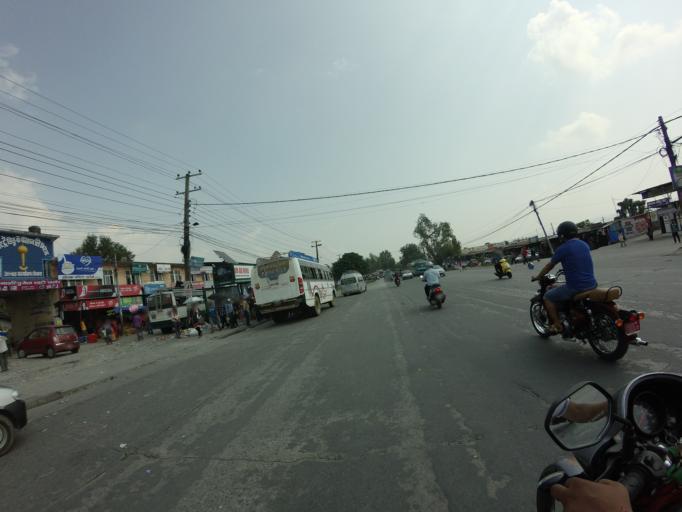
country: NP
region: Western Region
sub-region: Gandaki Zone
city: Pokhara
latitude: 28.2088
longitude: 83.9875
